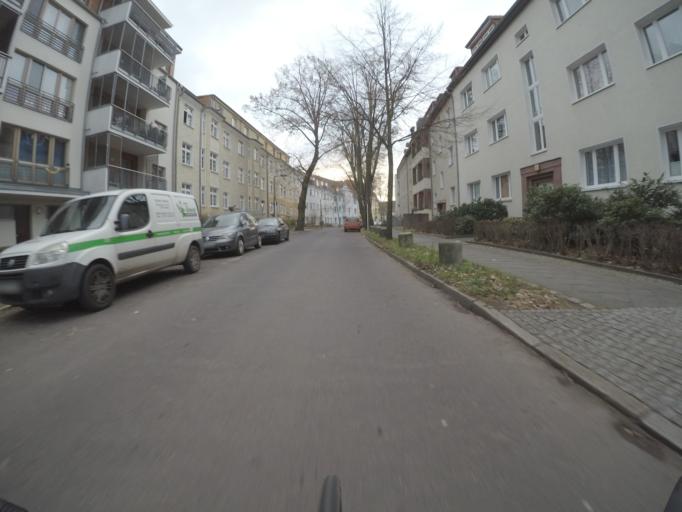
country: DE
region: Berlin
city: Karlshorst
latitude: 52.4827
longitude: 13.5284
